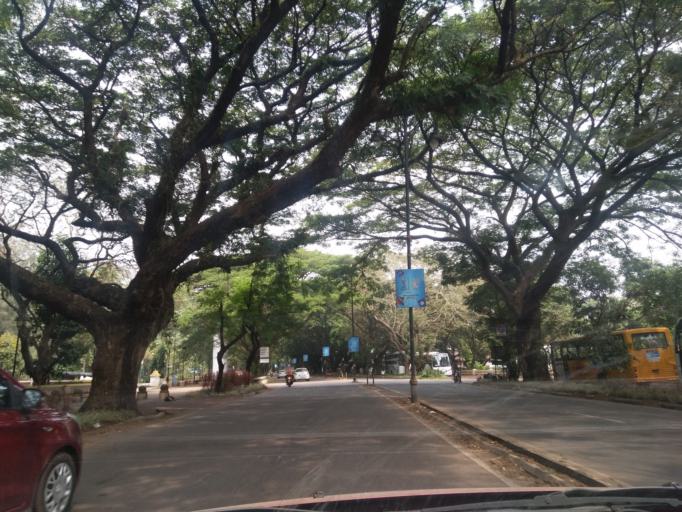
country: IN
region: Goa
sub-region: North Goa
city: Panaji
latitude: 15.4956
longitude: 73.8189
